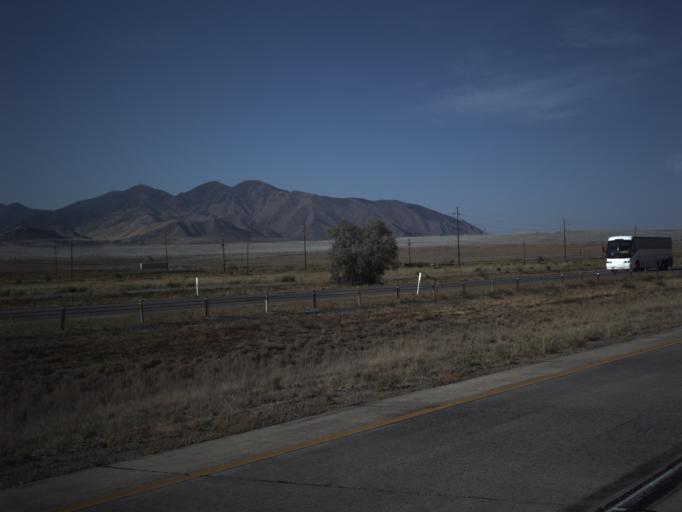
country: US
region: Utah
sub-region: Salt Lake County
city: Magna
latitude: 40.7711
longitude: -112.0784
